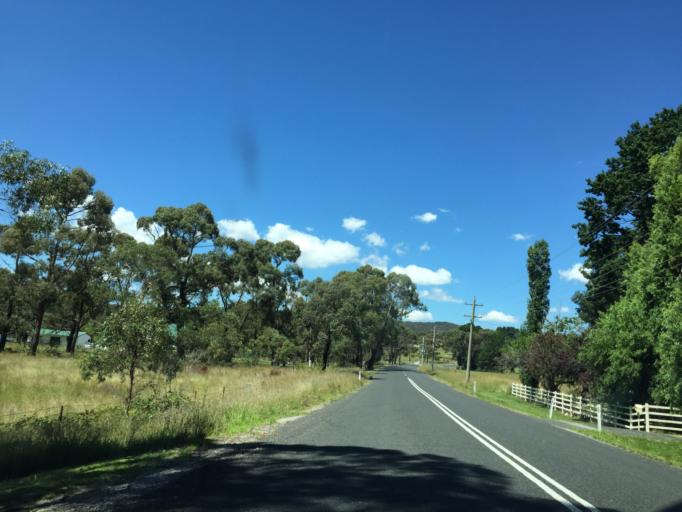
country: AU
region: New South Wales
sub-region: Lithgow
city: Lithgow
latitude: -33.4379
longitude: 150.1231
